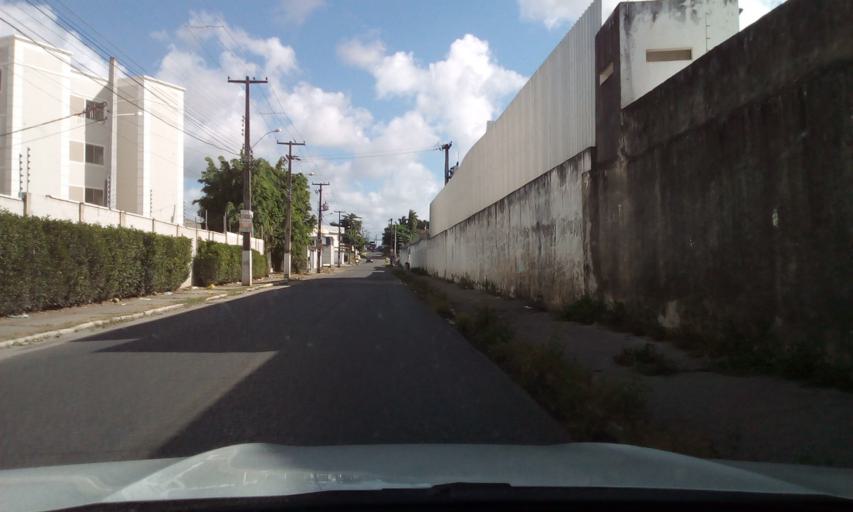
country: BR
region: Paraiba
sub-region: Bayeux
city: Bayeux
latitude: -7.1706
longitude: -34.8958
